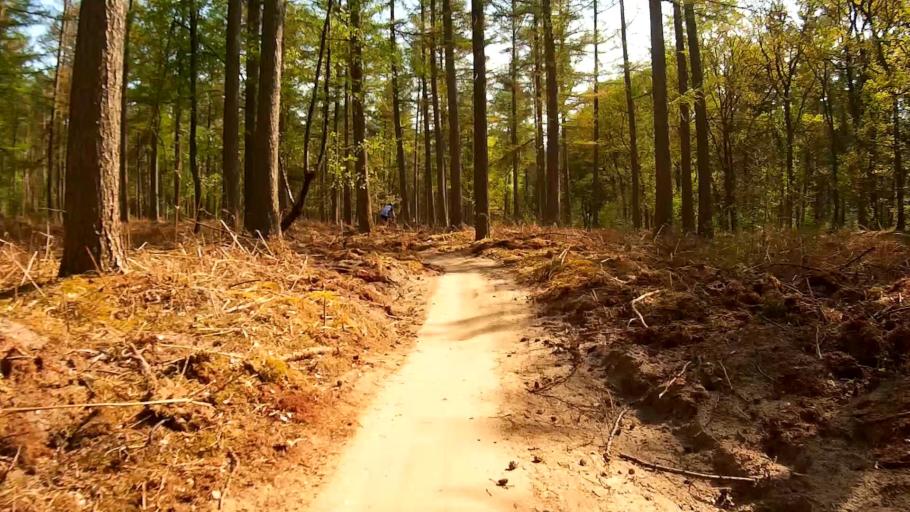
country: NL
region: Utrecht
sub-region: Gemeente Baarn
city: Baarn
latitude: 52.1935
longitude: 5.2345
